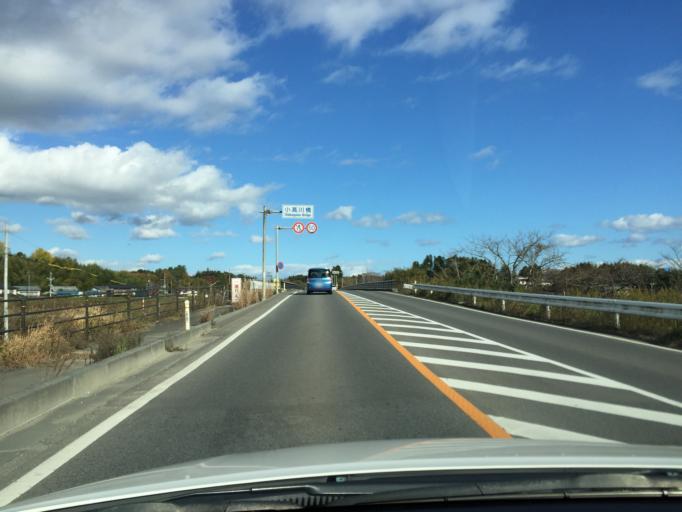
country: JP
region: Fukushima
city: Namie
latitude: 37.5645
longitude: 141.0027
